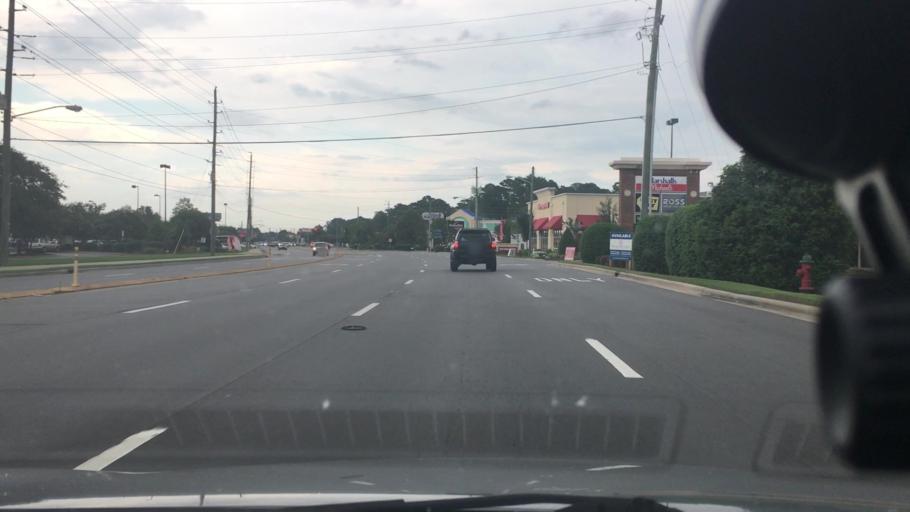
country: US
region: North Carolina
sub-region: Pitt County
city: Summerfield
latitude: 35.5751
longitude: -77.3848
